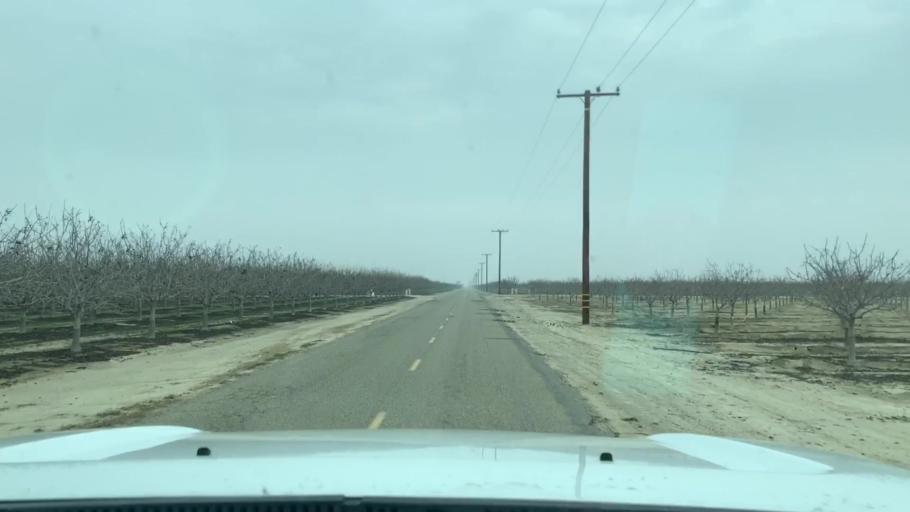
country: US
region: California
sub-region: Tulare County
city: Earlimart
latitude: 35.8193
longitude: -119.3500
